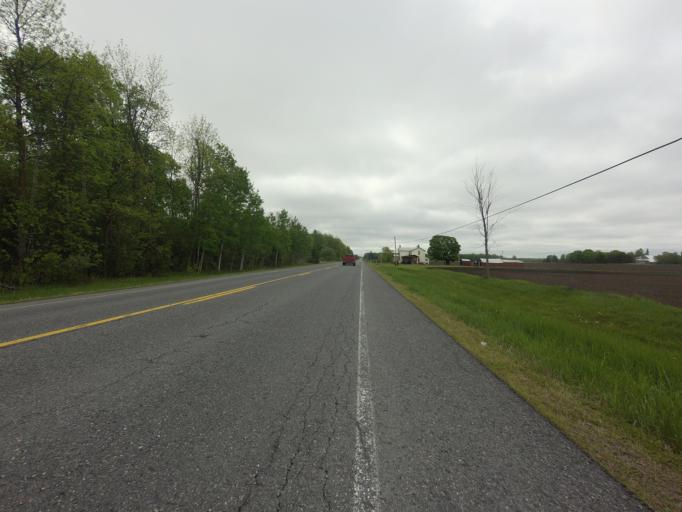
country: CA
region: Ontario
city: Casselman
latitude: 45.0490
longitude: -75.1982
